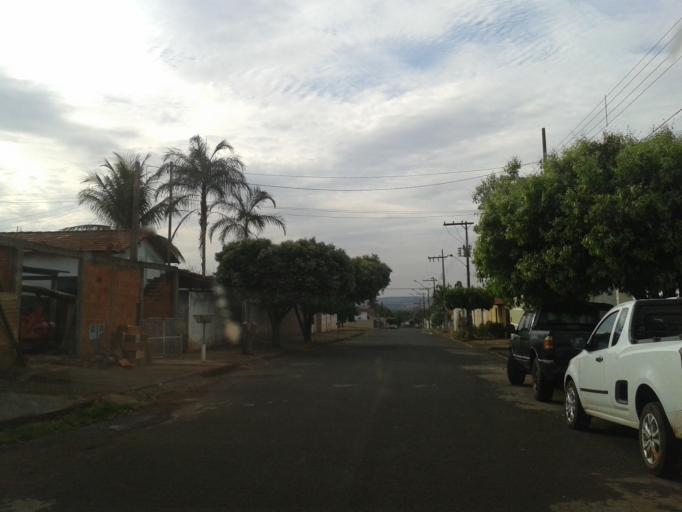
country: BR
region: Minas Gerais
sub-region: Ituiutaba
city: Ituiutaba
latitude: -18.9917
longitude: -49.4519
